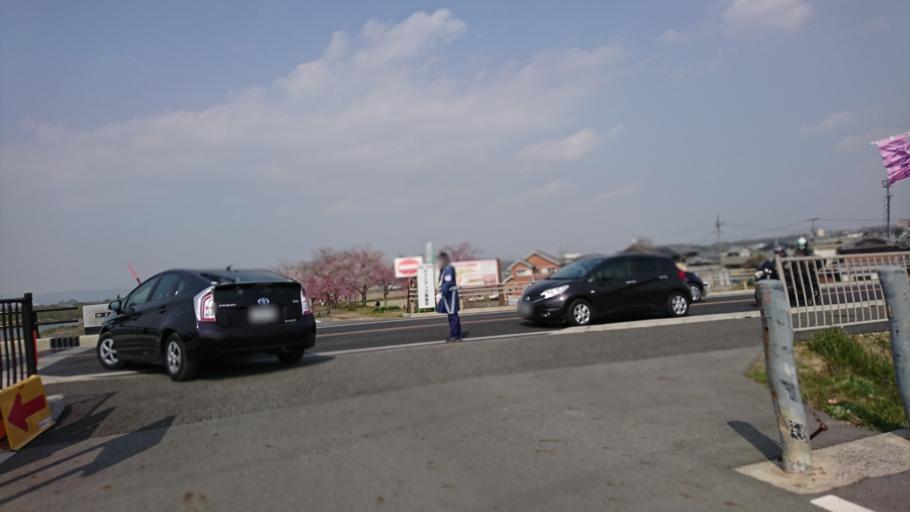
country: JP
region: Hyogo
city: Ono
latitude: 34.8614
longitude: 134.9178
